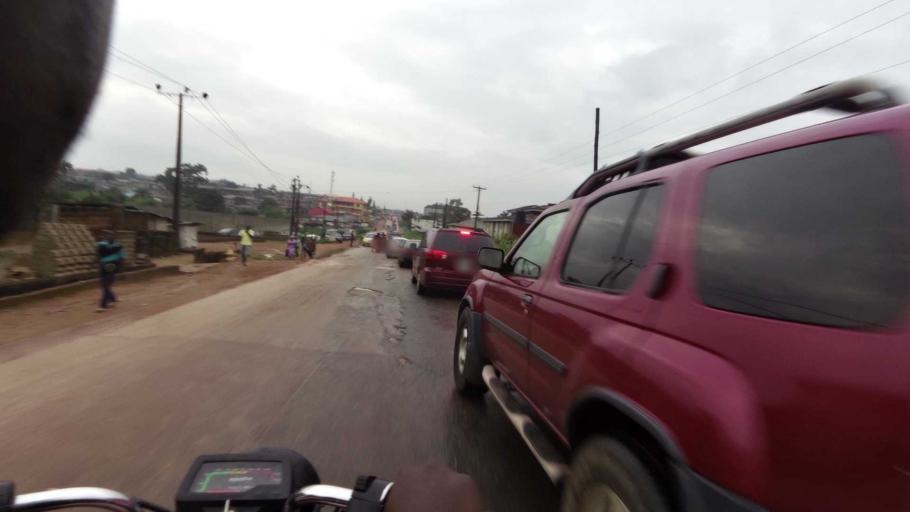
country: NG
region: Oyo
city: Ibadan
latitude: 7.4275
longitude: 3.9387
